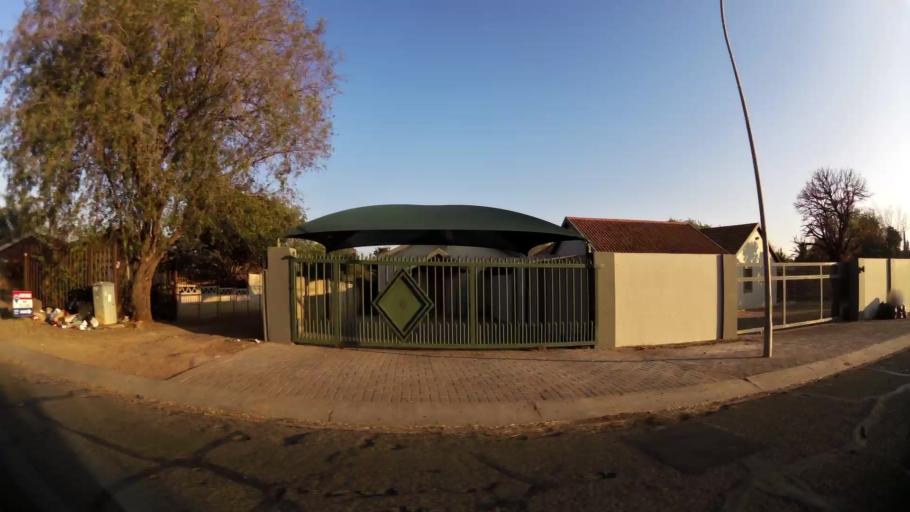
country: ZA
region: Orange Free State
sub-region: Mangaung Metropolitan Municipality
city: Bloemfontein
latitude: -29.0891
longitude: 26.1551
